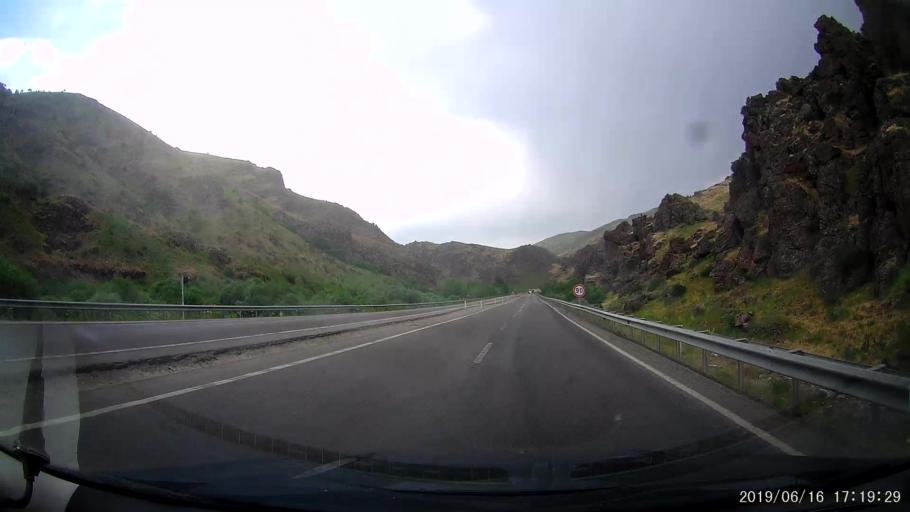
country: TR
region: Erzincan
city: Tercan
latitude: 39.8003
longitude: 40.5283
